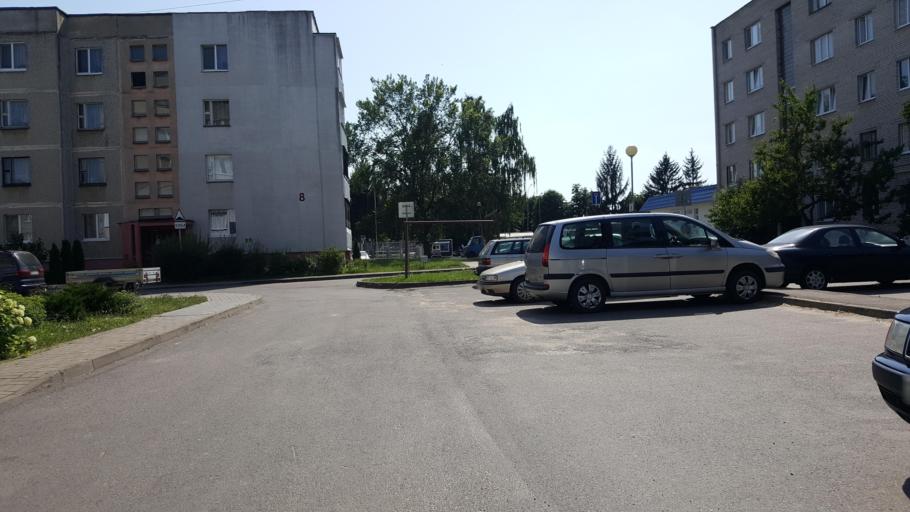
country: BY
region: Brest
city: Zhabinka
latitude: 52.1911
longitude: 24.0305
